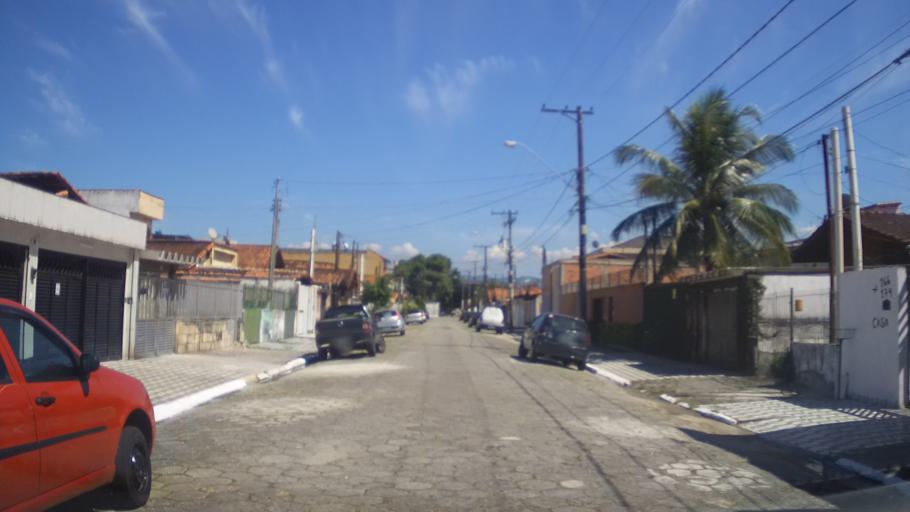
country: BR
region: Sao Paulo
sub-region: Praia Grande
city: Praia Grande
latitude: -24.0014
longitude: -46.4143
